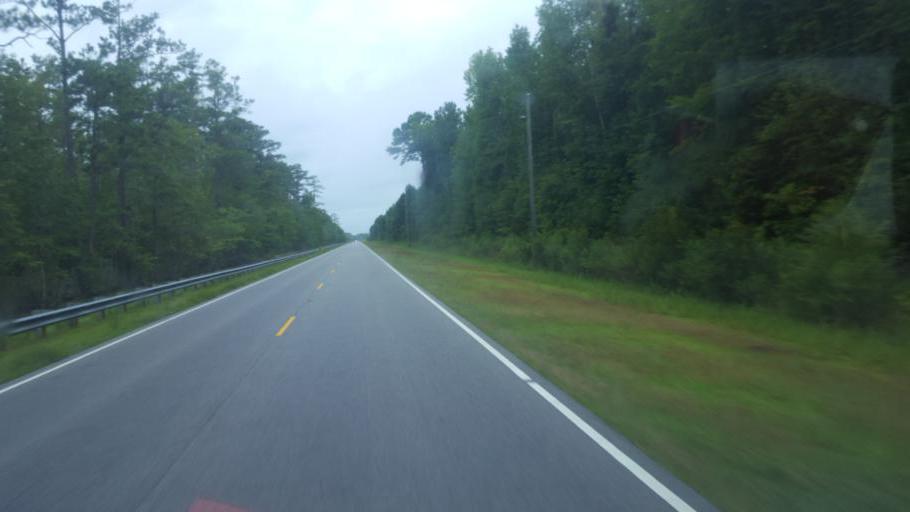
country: US
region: North Carolina
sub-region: Tyrrell County
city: Columbia
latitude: 35.9017
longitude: -76.0844
